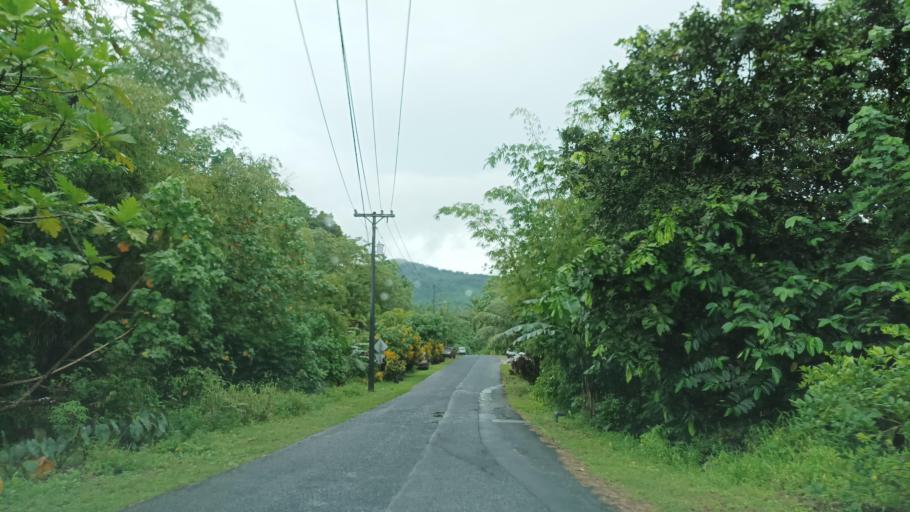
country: FM
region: Pohnpei
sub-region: Sokehs Municipality
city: Palikir - National Government Center
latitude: 6.8876
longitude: 158.1554
